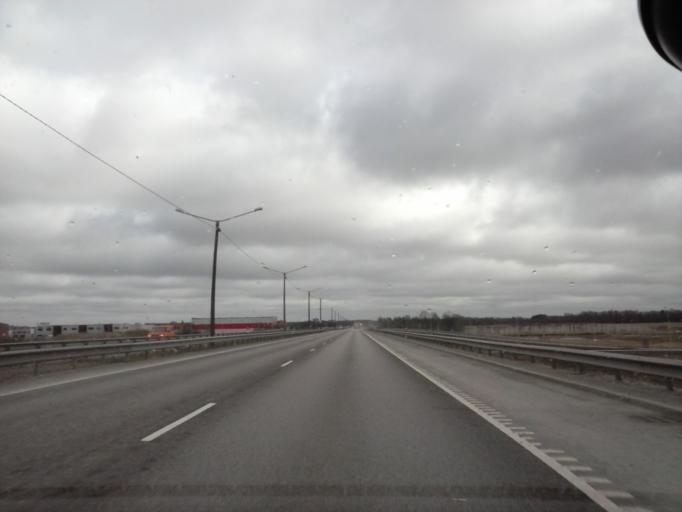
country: EE
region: Harju
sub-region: Rae vald
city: Jueri
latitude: 59.3531
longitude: 24.8823
